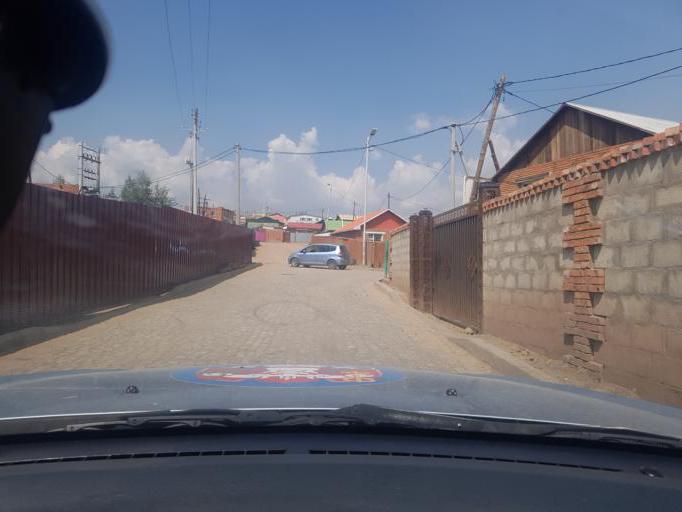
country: MN
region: Ulaanbaatar
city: Ulaanbaatar
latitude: 47.9350
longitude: 106.8953
